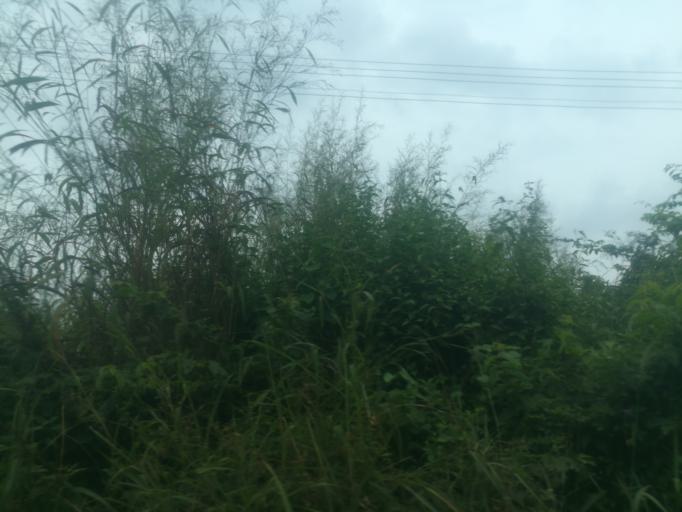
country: NG
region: Ogun
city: Itori
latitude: 7.0997
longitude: 3.1651
